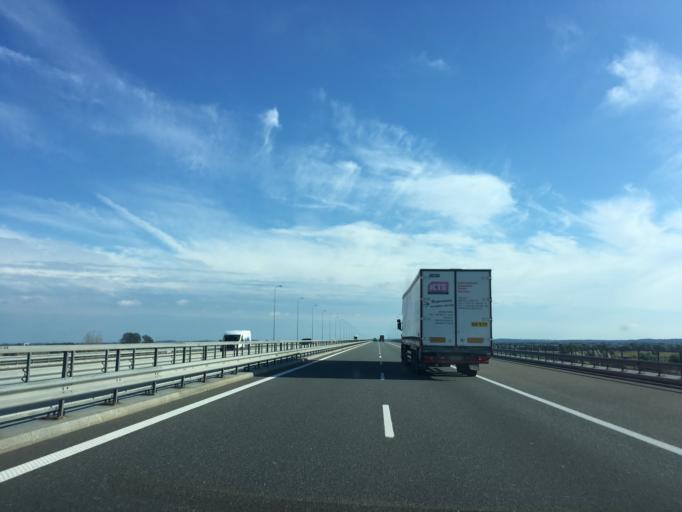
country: PL
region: Kujawsko-Pomorskie
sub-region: Grudziadz
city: Grudziadz
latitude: 53.4452
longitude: 18.6759
